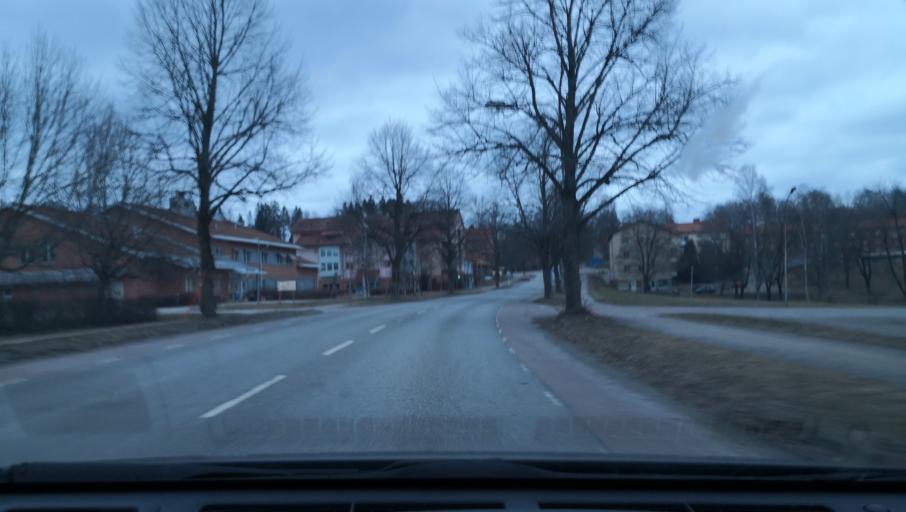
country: SE
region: Vaestmanland
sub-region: Kopings Kommun
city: Kolsva
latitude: 59.5995
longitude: 15.8385
